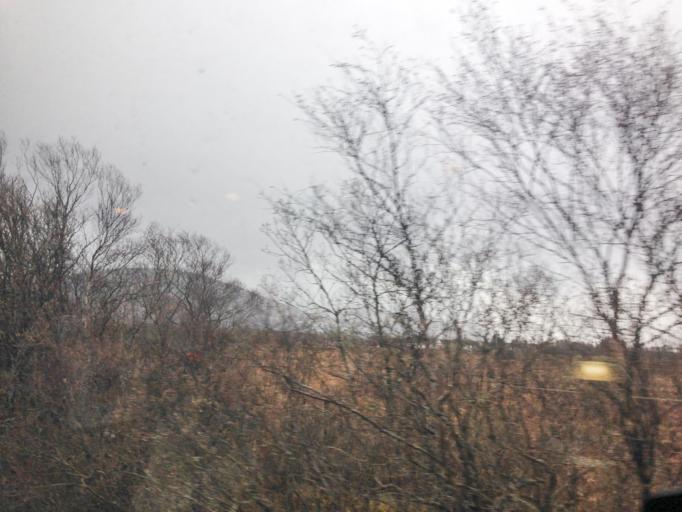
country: GB
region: Scotland
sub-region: Highland
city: Fort William
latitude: 56.8410
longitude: -5.0914
